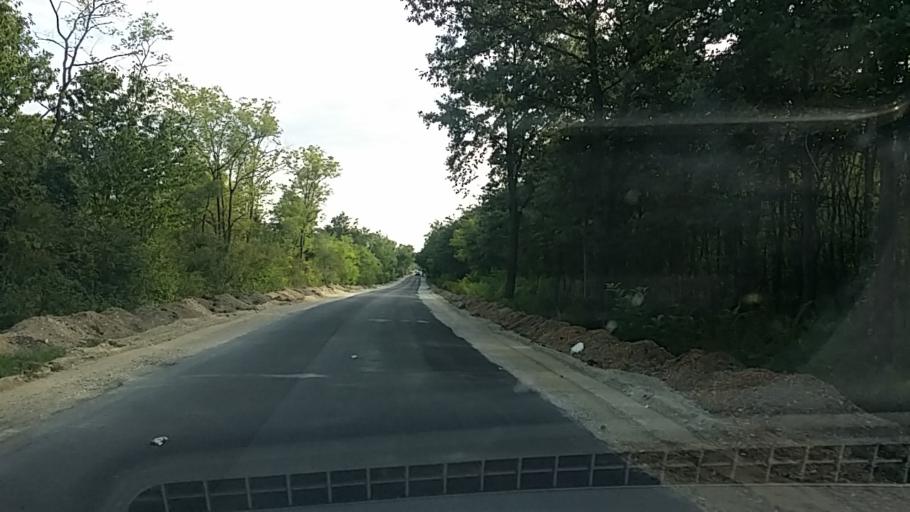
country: AT
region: Burgenland
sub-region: Eisenstadt-Umgebung
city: Morbisch am See
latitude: 47.7602
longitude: 16.6226
